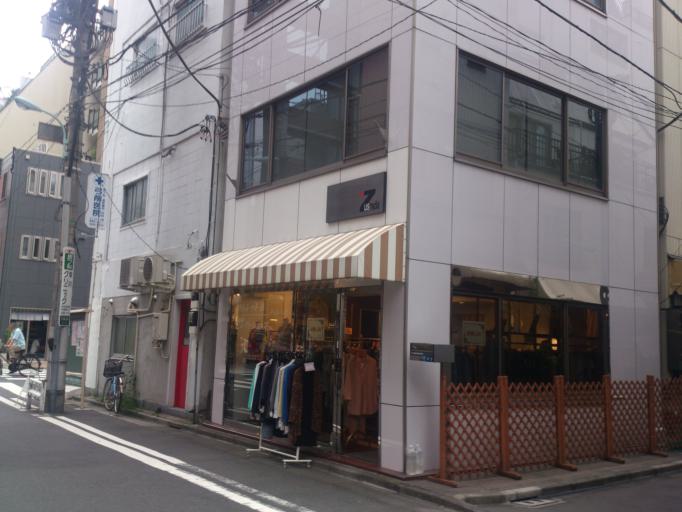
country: JP
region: Tokyo
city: Tokyo
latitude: 35.6852
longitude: 139.7841
